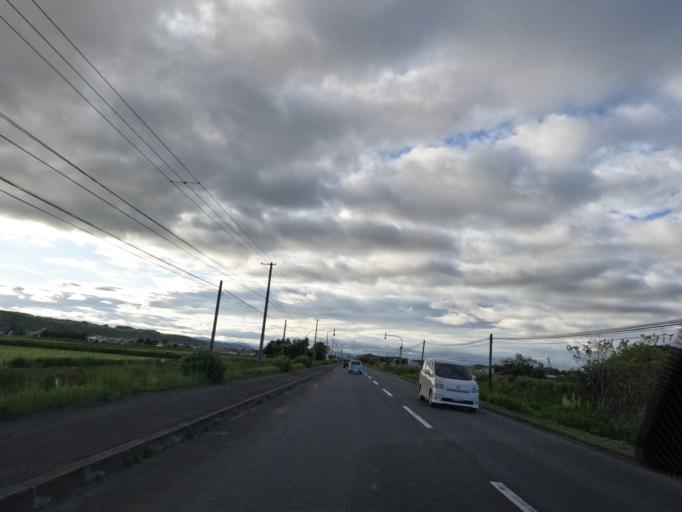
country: JP
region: Hokkaido
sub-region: Asahikawa-shi
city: Asahikawa
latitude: 43.6898
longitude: 142.3889
